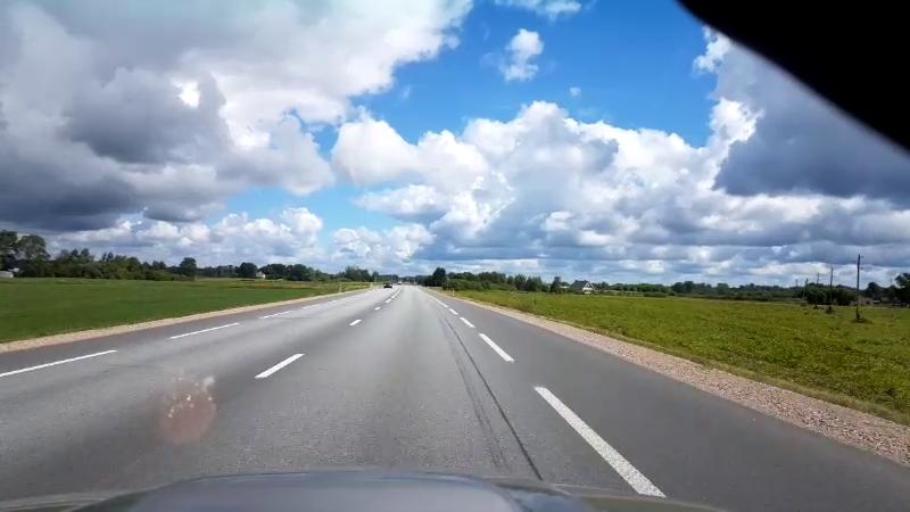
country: LV
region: Lecava
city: Iecava
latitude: 56.6133
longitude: 24.2152
